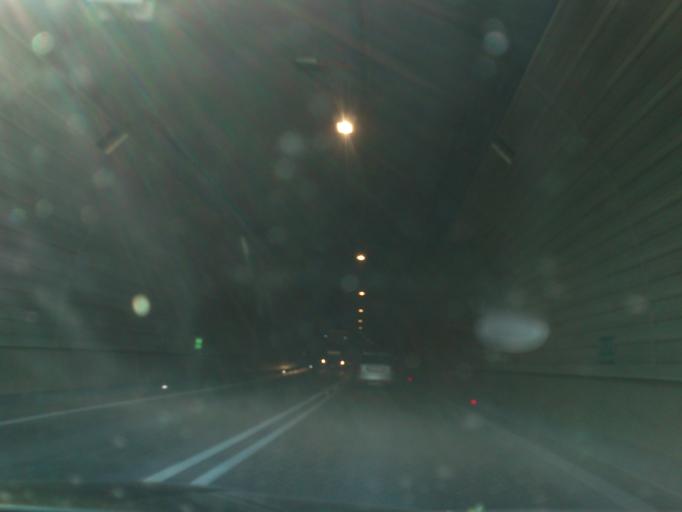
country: AT
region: Upper Austria
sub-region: Politischer Bezirk Urfahr-Umgebung
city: Alberndorf in der Riedmark
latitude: 48.4359
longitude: 14.4808
